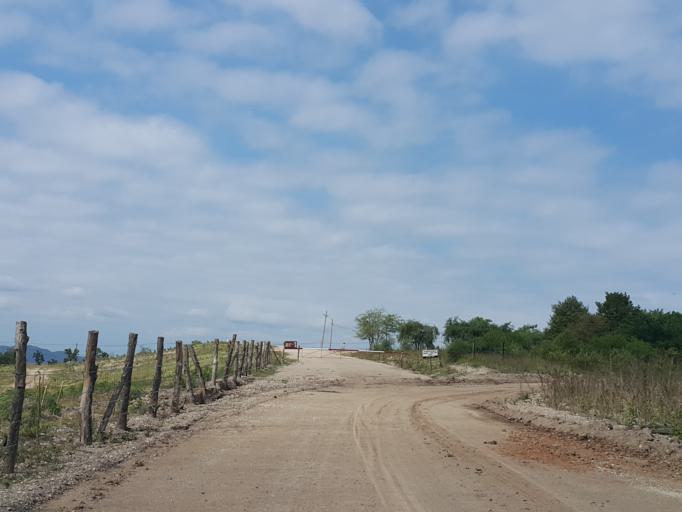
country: TH
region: Lampang
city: Mae Mo
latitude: 18.3341
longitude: 99.7542
